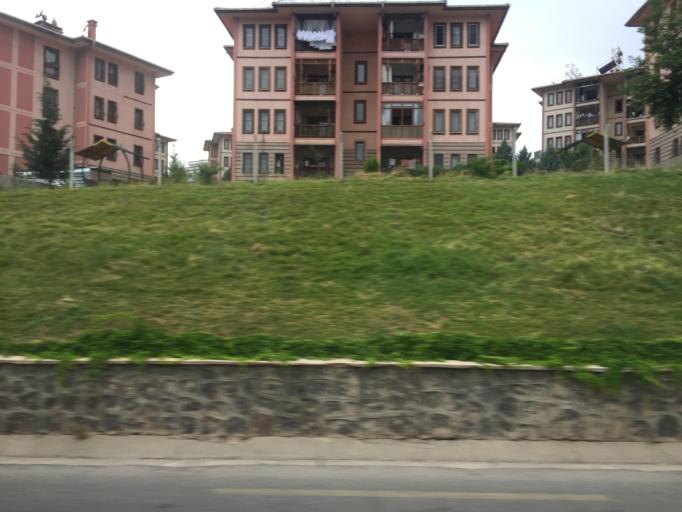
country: TR
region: Gaziantep
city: Gaziantep
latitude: 37.0426
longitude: 37.4245
